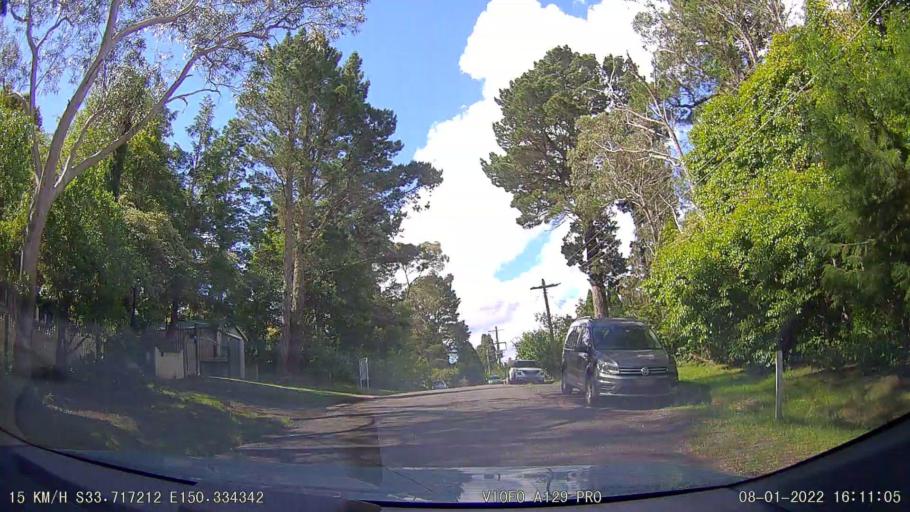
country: AU
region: New South Wales
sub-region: Blue Mountains Municipality
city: Leura
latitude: -33.7172
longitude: 150.3343
